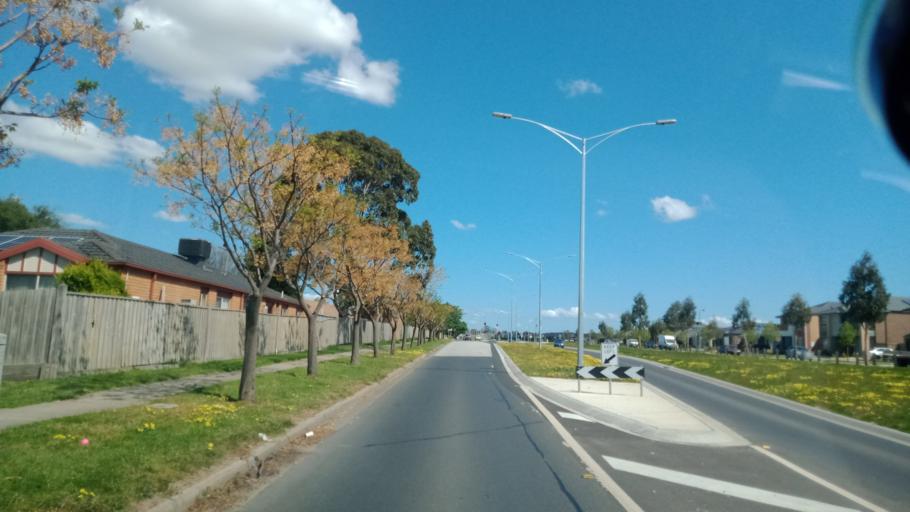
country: AU
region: Victoria
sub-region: Casey
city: Cranbourne West
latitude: -38.0997
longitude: 145.2544
